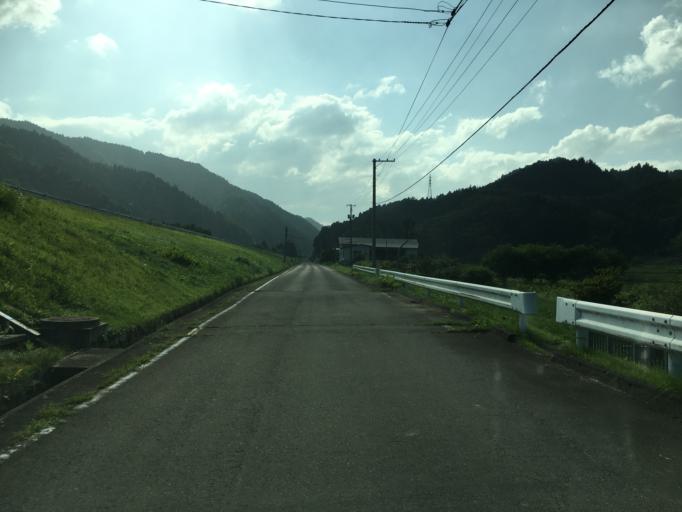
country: JP
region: Miyagi
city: Marumori
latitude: 37.9316
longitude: 140.7344
